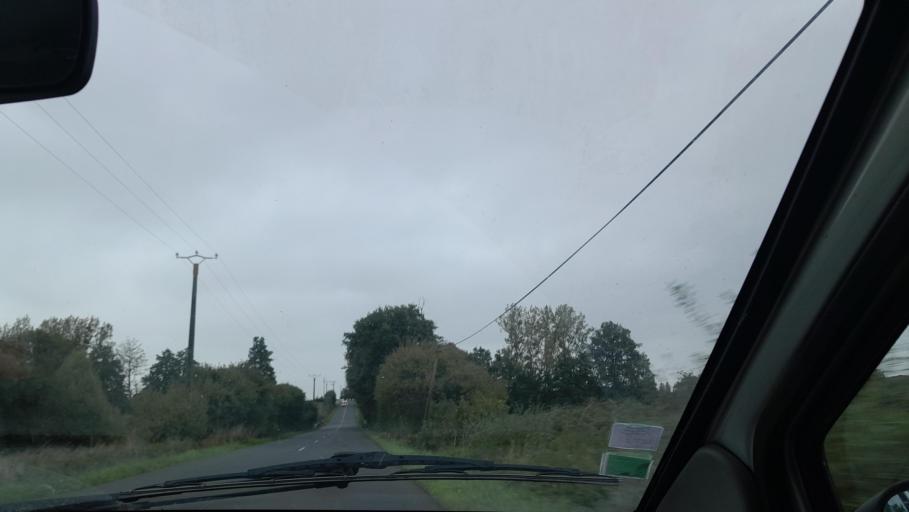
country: FR
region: Pays de la Loire
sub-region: Departement de Maine-et-Loire
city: Pouance
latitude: 47.7216
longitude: -1.1778
